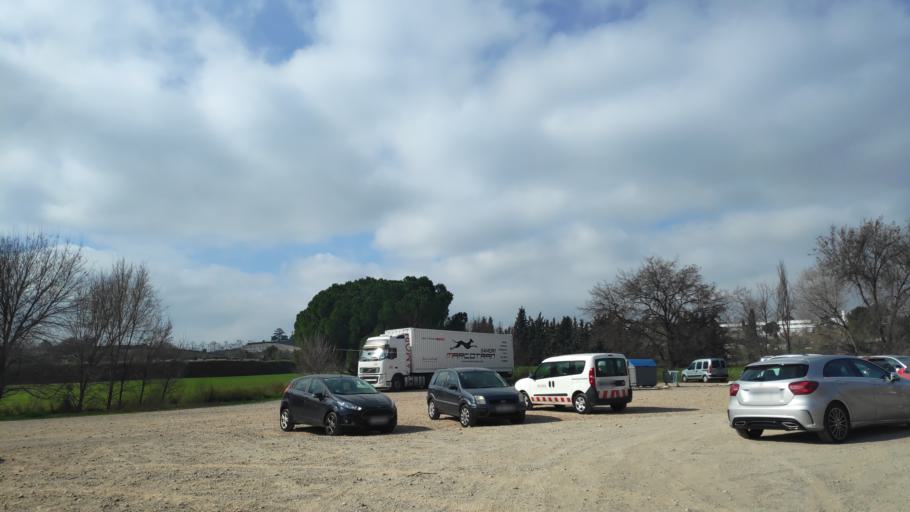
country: ES
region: Catalonia
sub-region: Provincia de Barcelona
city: Sant Quirze del Valles
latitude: 41.5550
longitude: 2.0825
